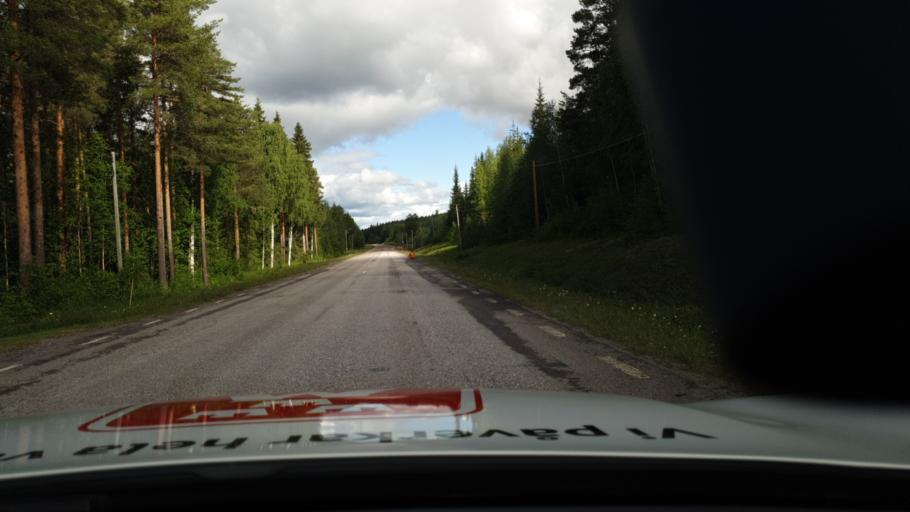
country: SE
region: Norrbotten
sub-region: Alvsbyns Kommun
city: AElvsbyn
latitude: 66.1151
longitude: 20.9271
